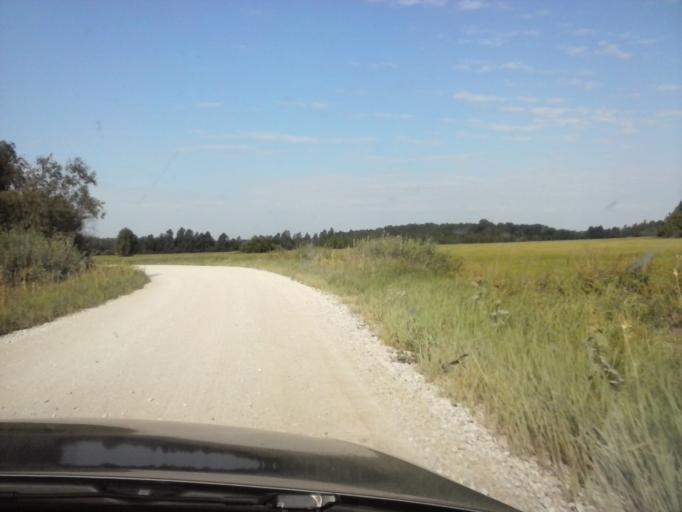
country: EE
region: Laeaene
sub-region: Ridala Parish
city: Uuemoisa
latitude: 58.8819
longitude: 23.5965
